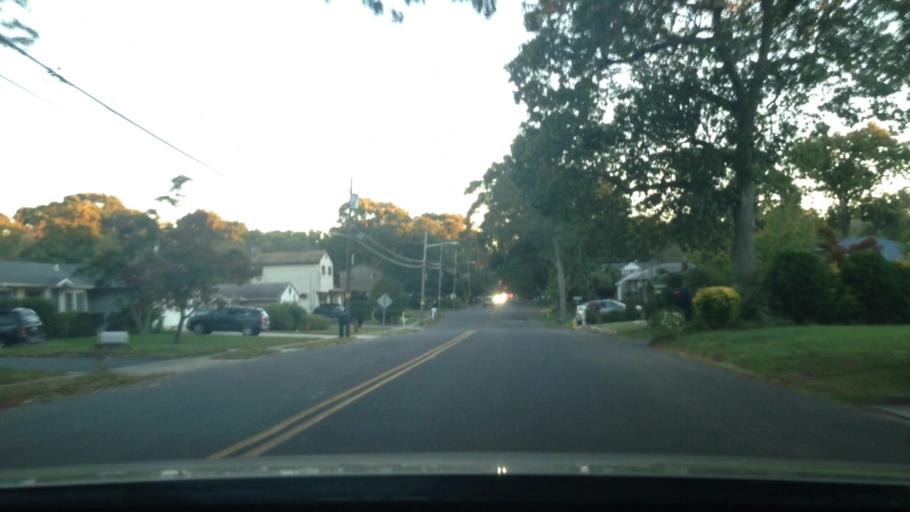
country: US
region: New York
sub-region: Suffolk County
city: Selden
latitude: 40.8600
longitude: -73.0344
